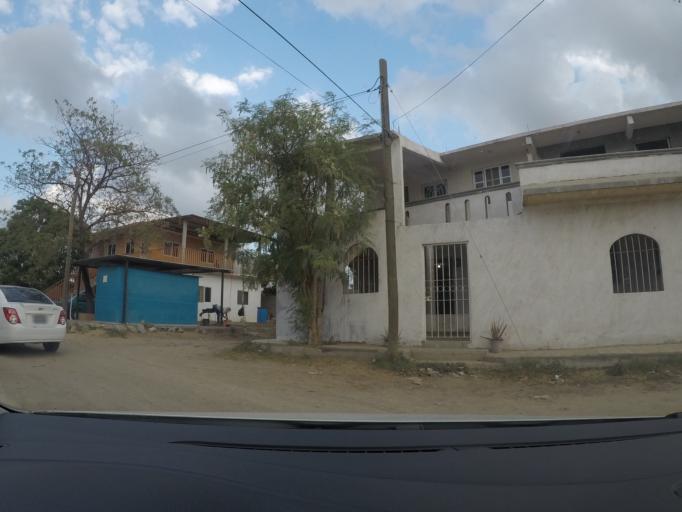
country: MX
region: Oaxaca
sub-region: Salina Cruz
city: Salina Cruz
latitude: 16.2116
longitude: -95.1989
